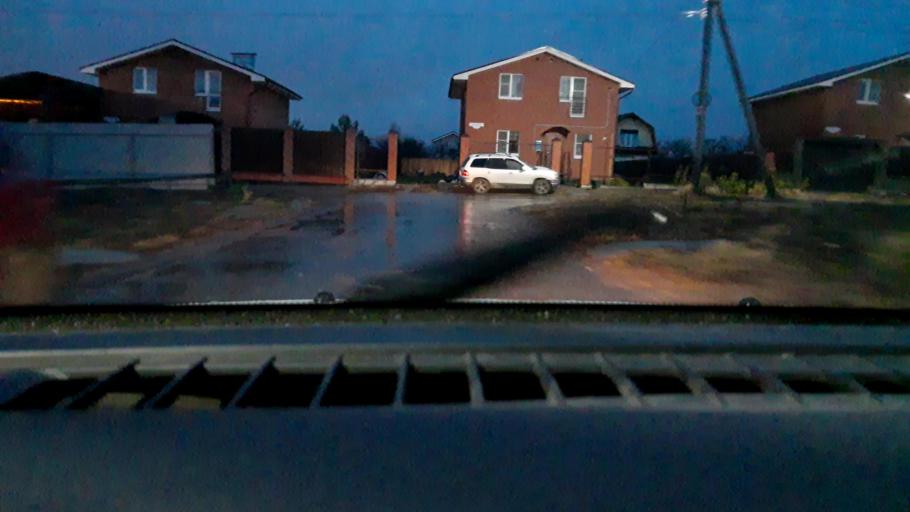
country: RU
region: Nizjnij Novgorod
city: Afonino
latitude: 56.2070
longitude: 44.1302
